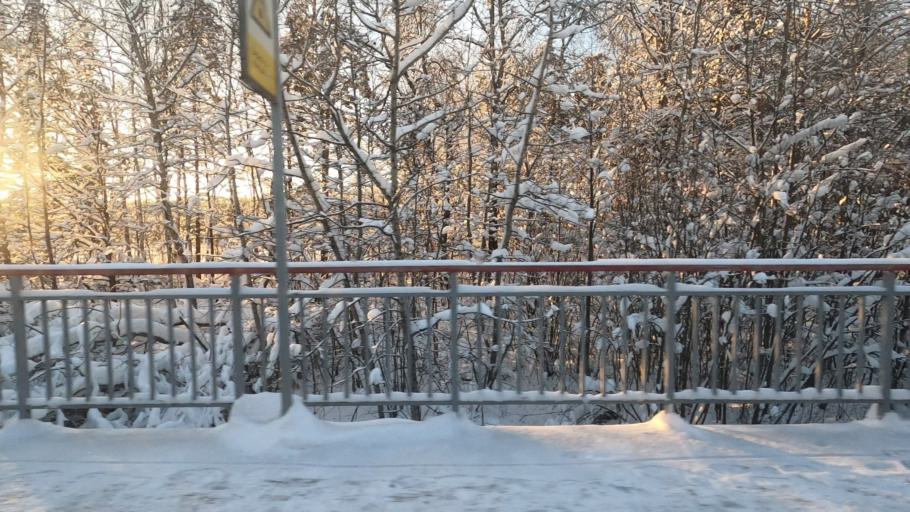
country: RU
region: Moskovskaya
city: Novo-Nikol'skoye
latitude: 56.6386
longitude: 37.5617
